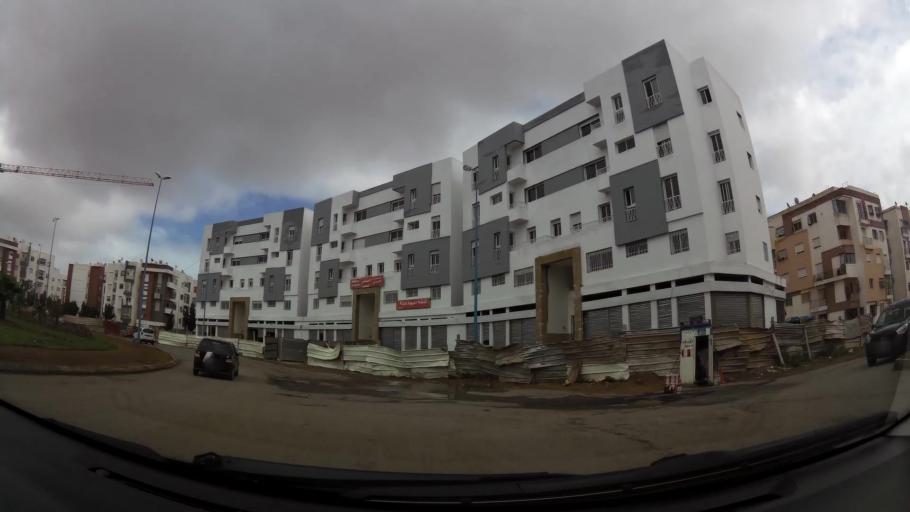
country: MA
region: Grand Casablanca
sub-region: Casablanca
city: Casablanca
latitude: 33.5387
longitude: -7.6926
